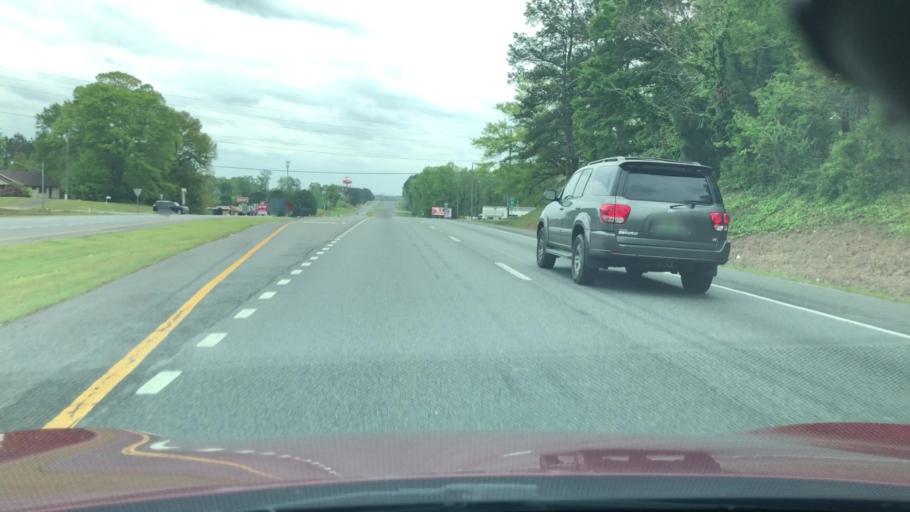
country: US
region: Alabama
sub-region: Tallapoosa County
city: Alexander City
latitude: 32.9418
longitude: -85.9813
